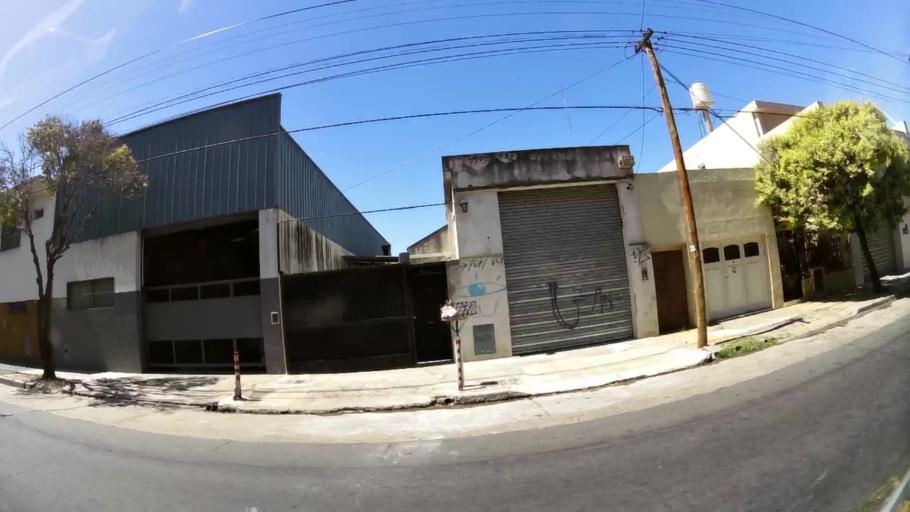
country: AR
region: Buenos Aires
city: Caseros
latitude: -34.5864
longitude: -58.5512
